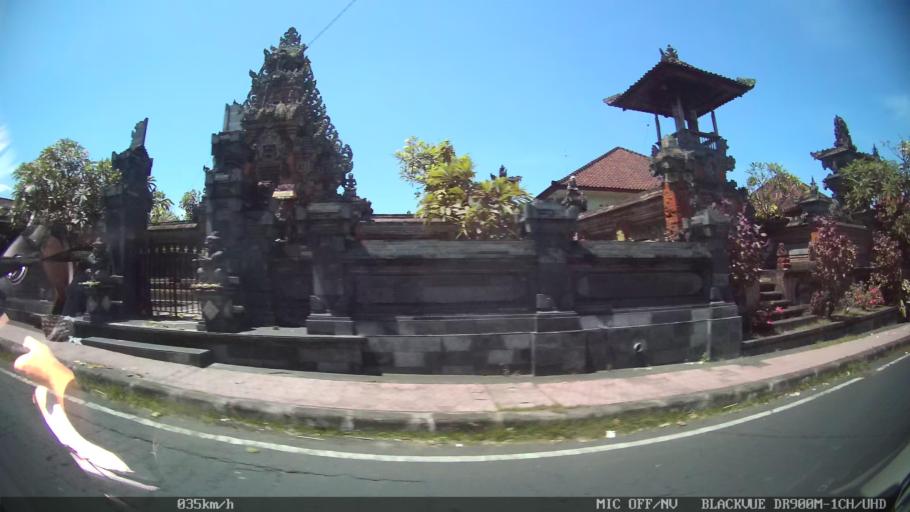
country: ID
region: Bali
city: Klungkung
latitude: -8.5762
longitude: 115.3504
